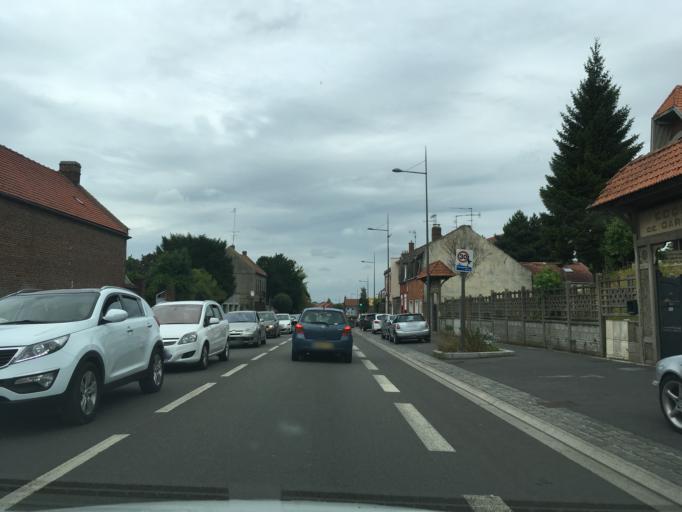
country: FR
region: Nord-Pas-de-Calais
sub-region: Departement du Nord
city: Cambrai
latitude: 50.1623
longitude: 3.2270
